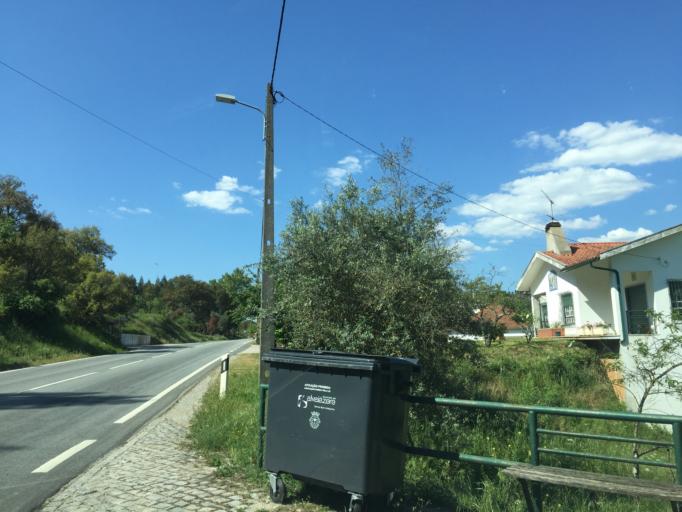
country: PT
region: Leiria
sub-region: Alvaiazere
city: Alvaiazere
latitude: 39.8535
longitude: -8.3455
